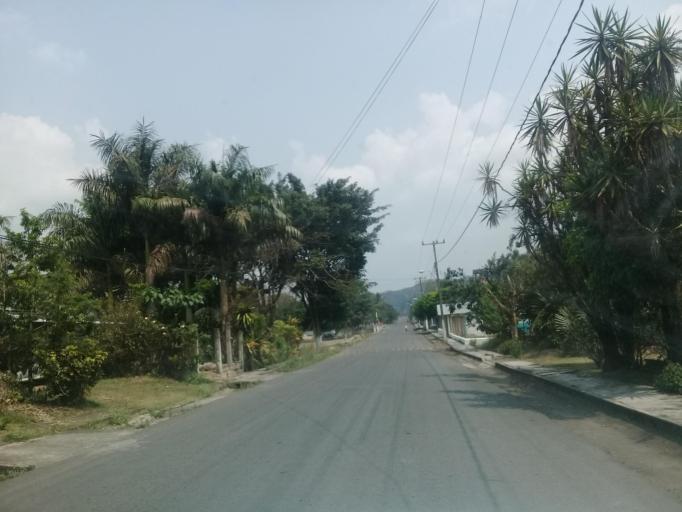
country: MX
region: Veracruz
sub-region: Cordoba
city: San Jose de Tapia
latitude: 18.8162
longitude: -96.9824
